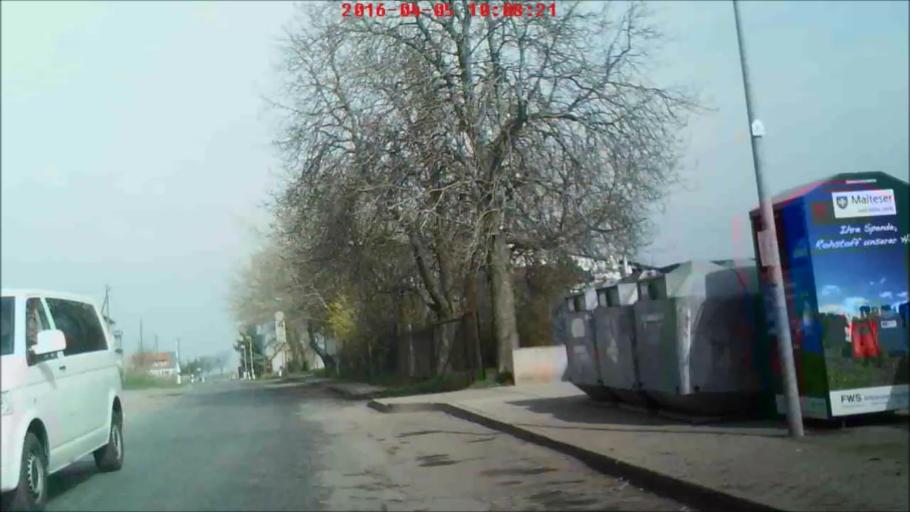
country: DE
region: Thuringia
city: Elxleben
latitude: 51.0230
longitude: 10.9499
